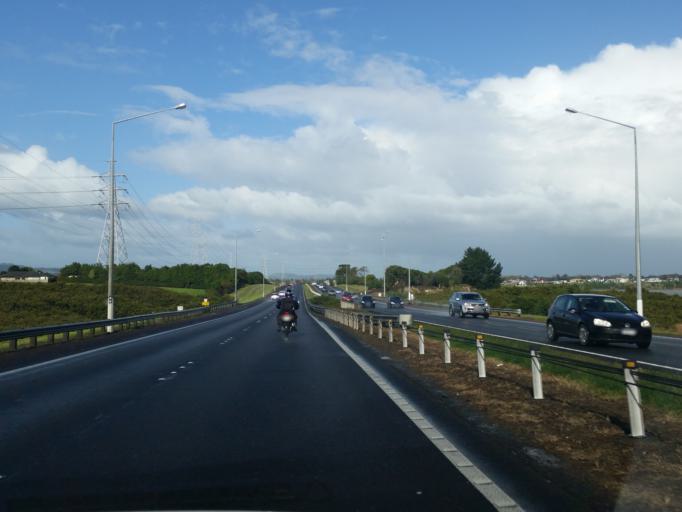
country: NZ
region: Auckland
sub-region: Auckland
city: Takanini
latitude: -37.0512
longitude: 174.9174
